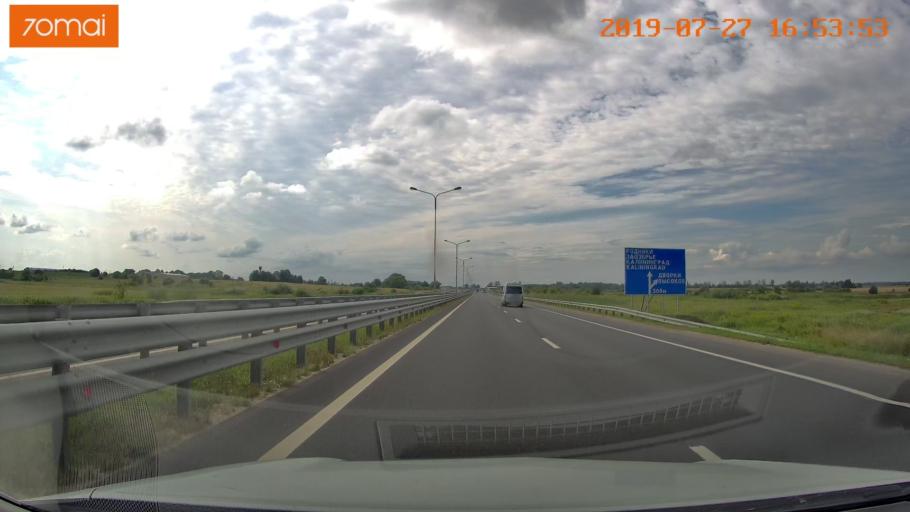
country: RU
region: Kaliningrad
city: Bol'shoe Isakovo
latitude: 54.6907
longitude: 20.8220
